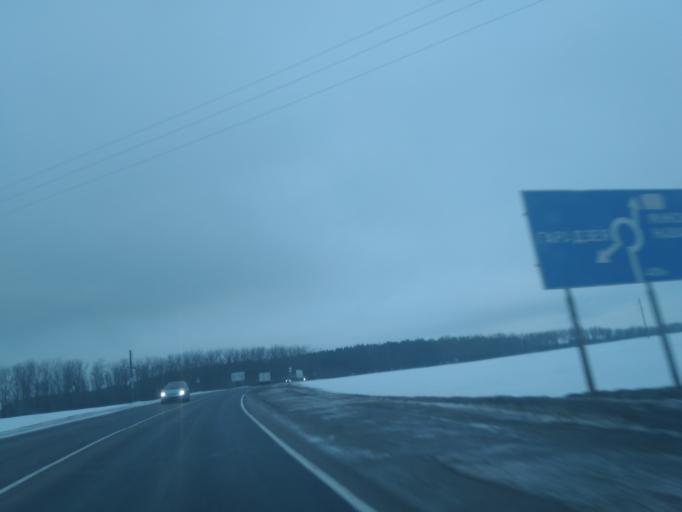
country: BY
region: Minsk
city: Haradzyeya
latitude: 53.3331
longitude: 26.5269
